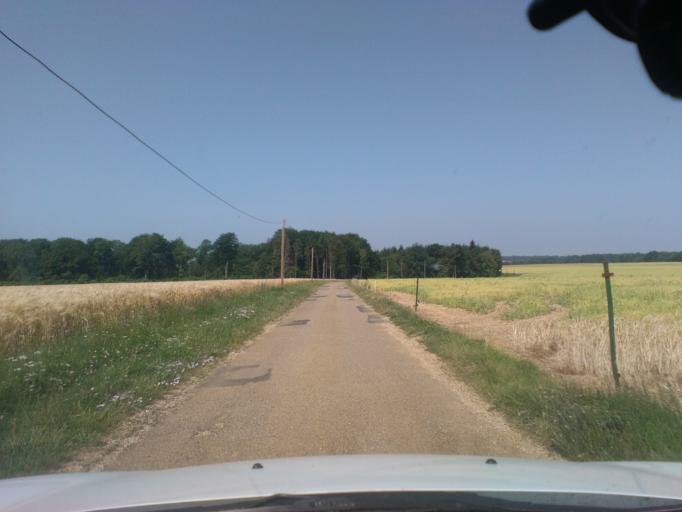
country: FR
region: Lorraine
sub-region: Departement des Vosges
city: Liffol-le-Grand
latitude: 48.3105
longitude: 5.4284
